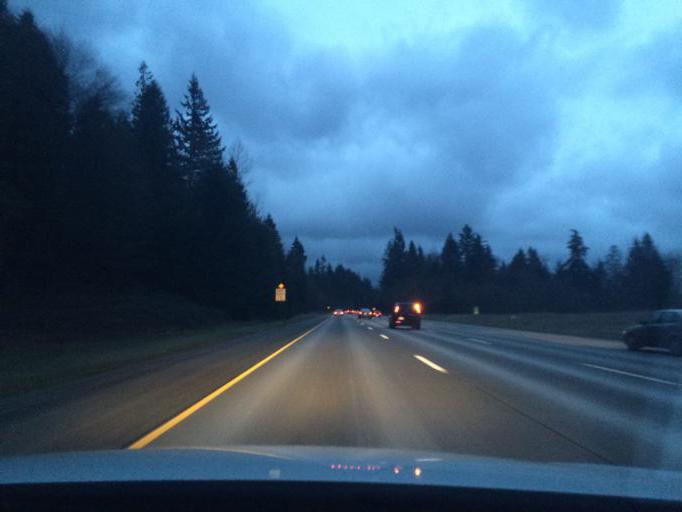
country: US
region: Washington
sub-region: King County
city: Fall City
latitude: 47.5140
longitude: -121.9159
